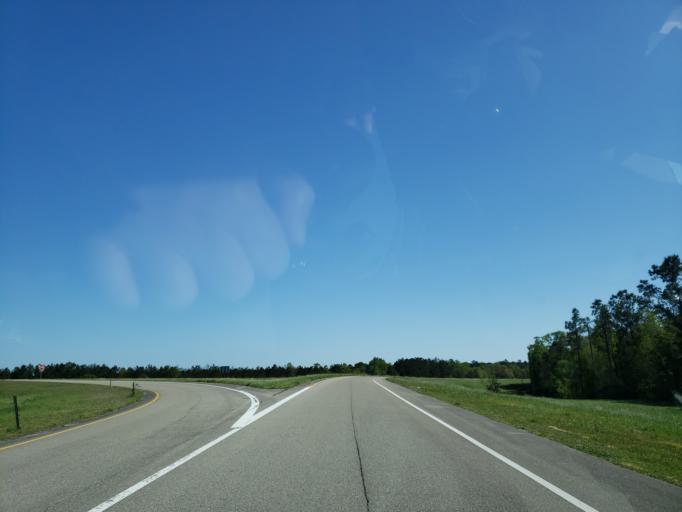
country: US
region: Mississippi
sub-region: Harrison County
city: Lyman
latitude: 30.5527
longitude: -89.0286
